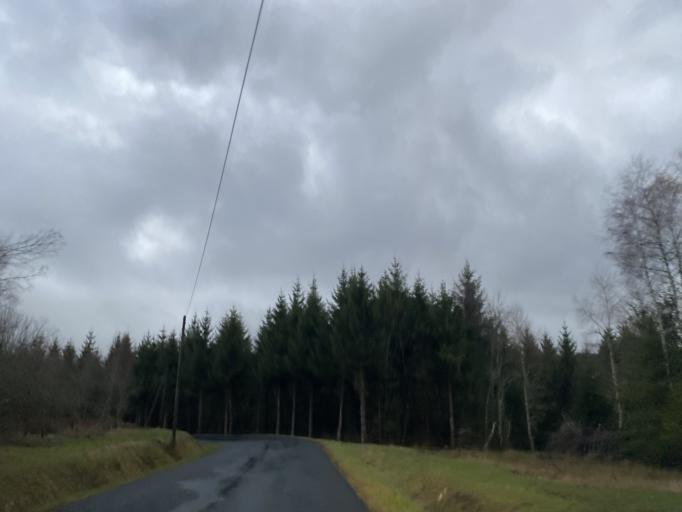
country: FR
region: Auvergne
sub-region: Departement du Puy-de-Dome
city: Cunlhat
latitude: 45.5427
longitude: 3.5774
